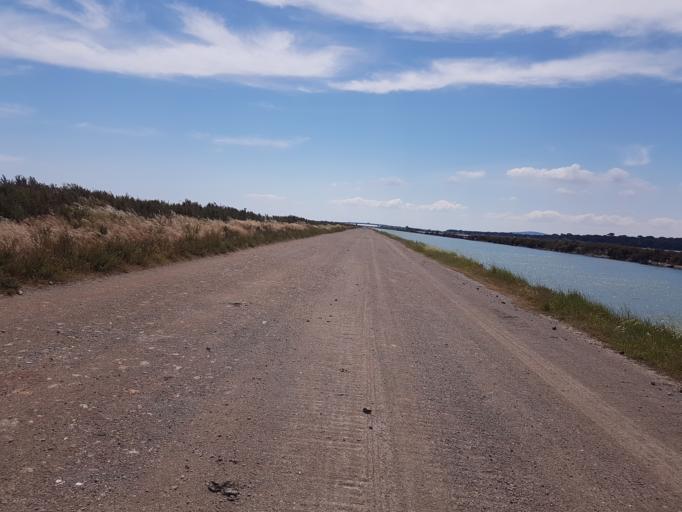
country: FR
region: Languedoc-Roussillon
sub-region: Departement de l'Herault
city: Vic-la-Gardiole
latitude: 43.4730
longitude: 3.8270
